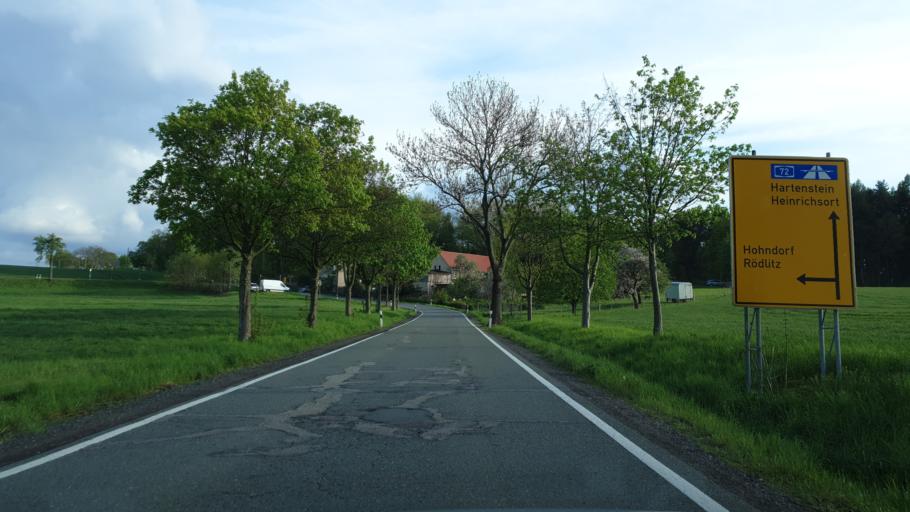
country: DE
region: Saxony
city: Lichtenstein
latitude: 50.7372
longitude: 12.6342
